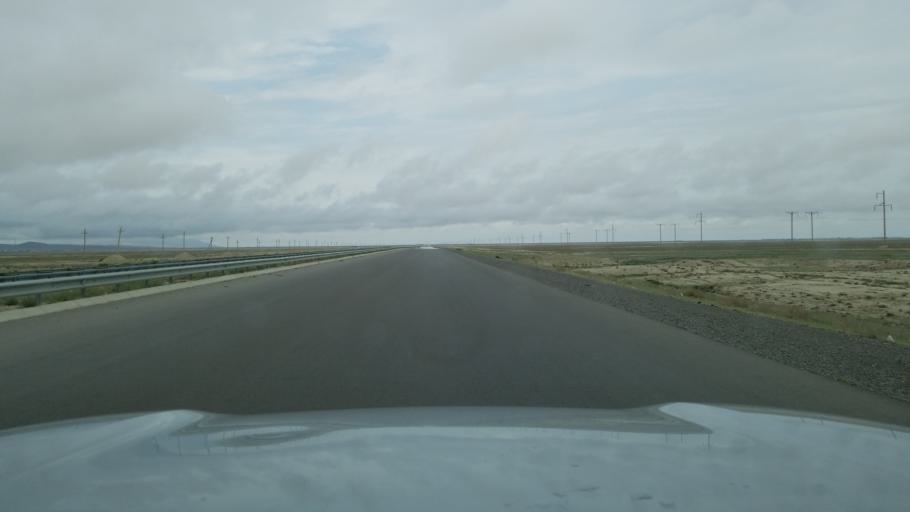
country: TM
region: Balkan
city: Serdar
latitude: 39.1131
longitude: 55.9201
